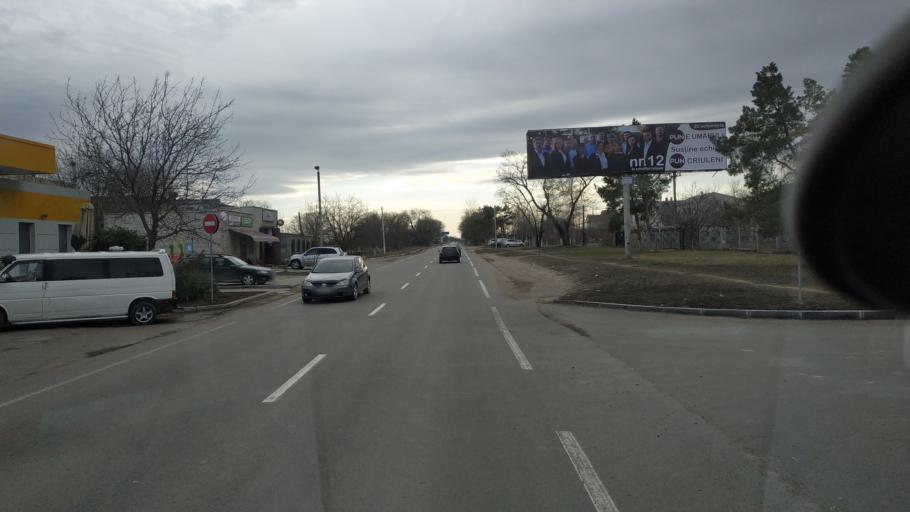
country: MD
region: Criuleni
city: Criuleni
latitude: 47.2030
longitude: 29.1554
